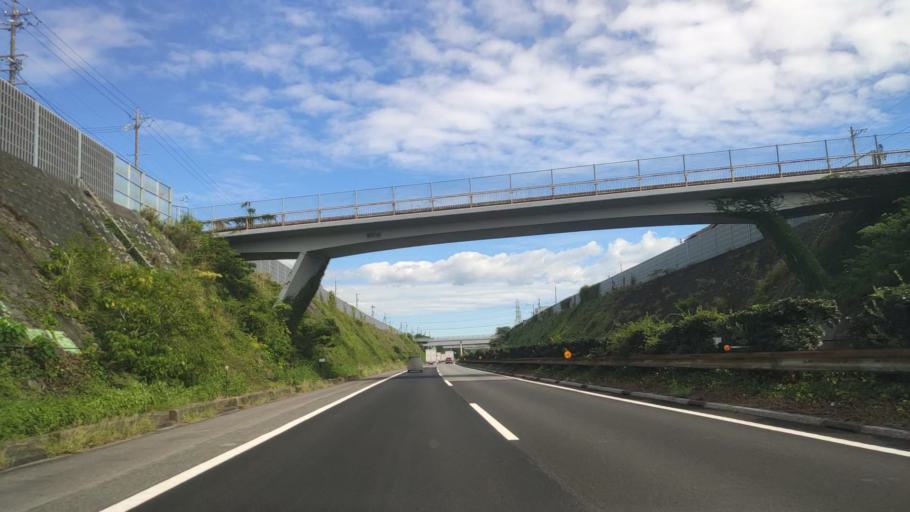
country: JP
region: Shizuoka
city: Hamamatsu
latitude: 34.7640
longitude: 137.7237
